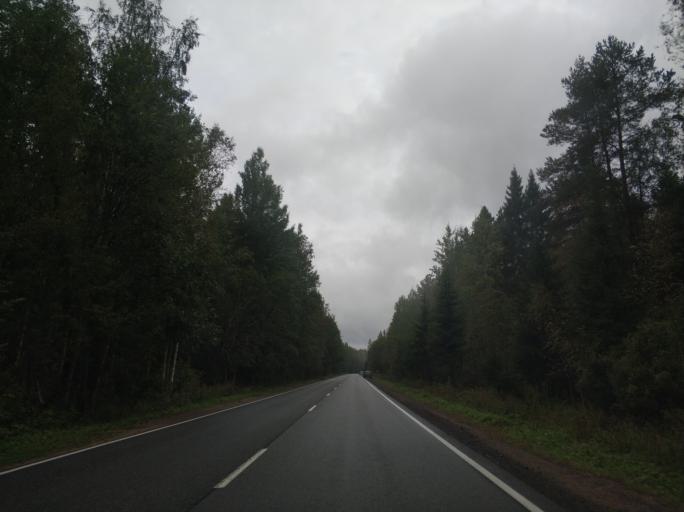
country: RU
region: Leningrad
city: Borisova Griva
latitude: 60.1571
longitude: 30.9281
